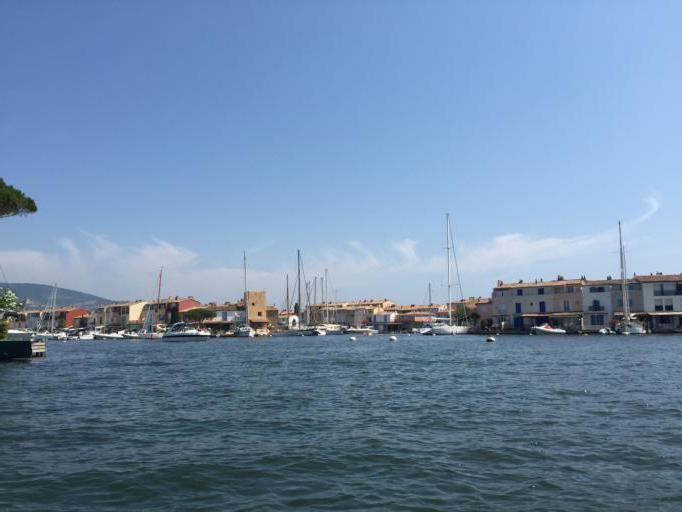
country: FR
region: Provence-Alpes-Cote d'Azur
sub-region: Departement du Var
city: Gassin
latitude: 43.2720
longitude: 6.5815
